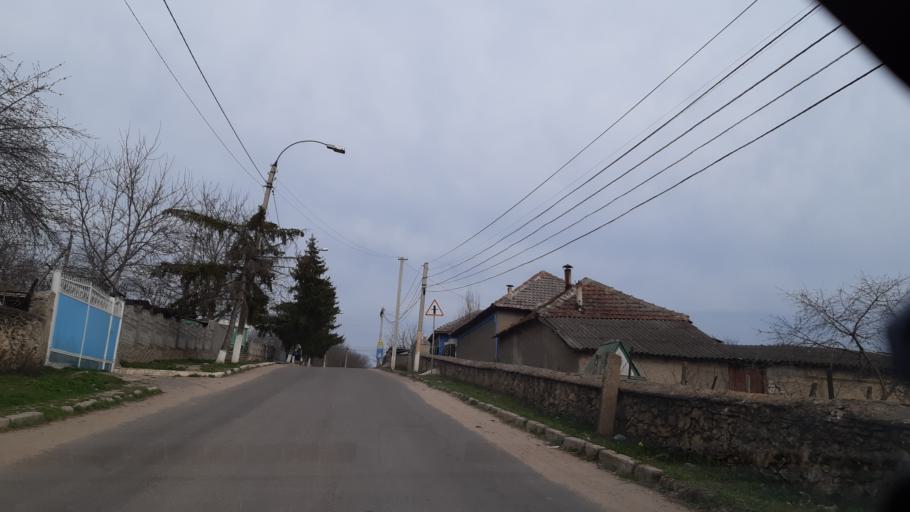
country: MD
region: Soldanesti
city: Soldanesti
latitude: 47.6842
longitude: 28.7663
